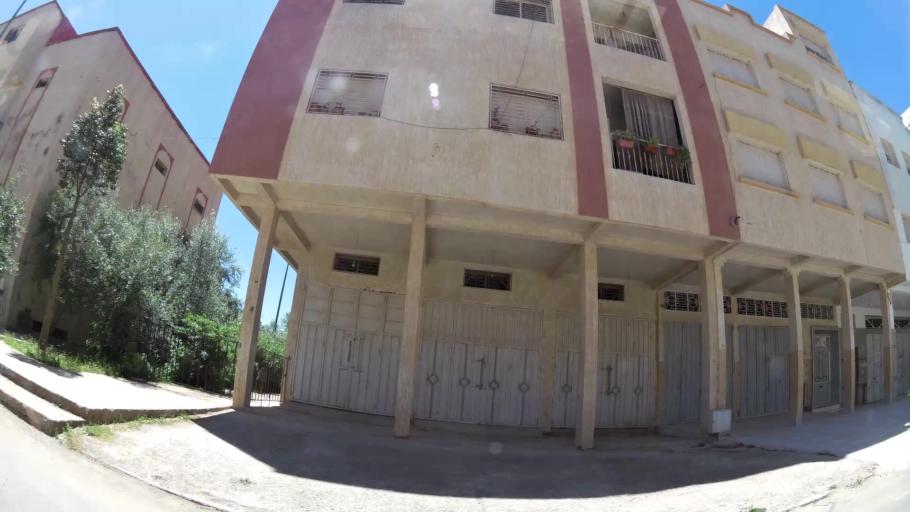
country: MA
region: Meknes-Tafilalet
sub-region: Meknes
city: Meknes
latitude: 33.8499
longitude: -5.5550
